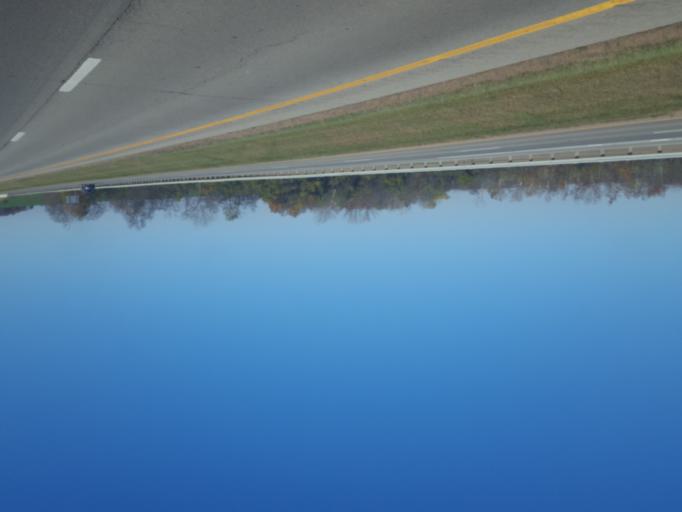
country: US
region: Ohio
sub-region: Wyandot County
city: Upper Sandusky
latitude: 40.7849
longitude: -83.2441
